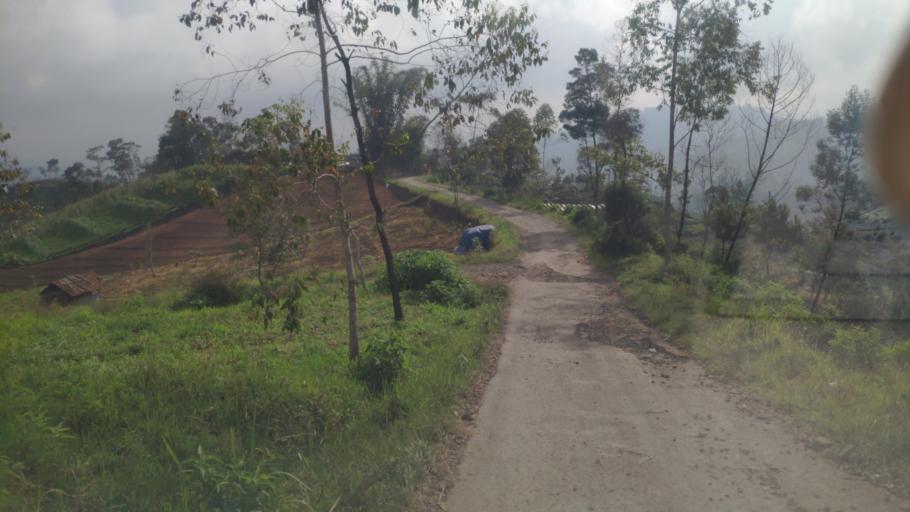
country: ID
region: Central Java
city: Wonosobo
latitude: -7.2655
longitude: 109.8360
